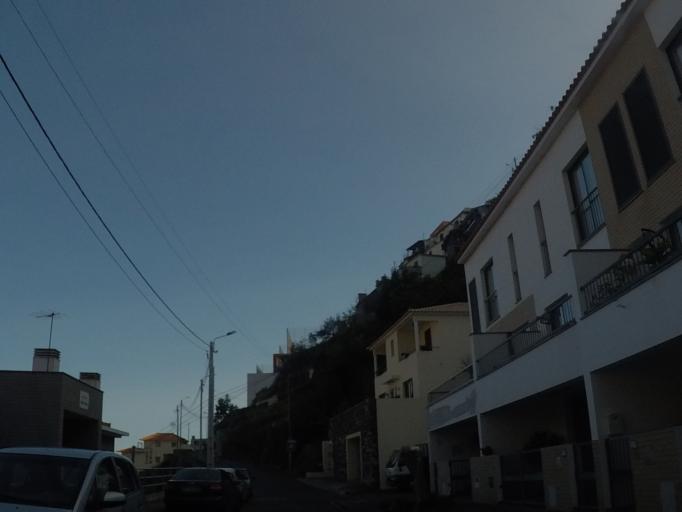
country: PT
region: Madeira
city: Camara de Lobos
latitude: 32.6564
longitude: -16.9915
